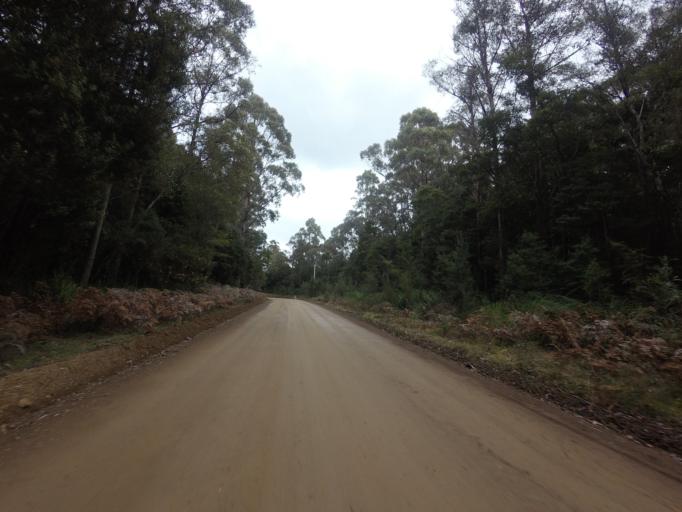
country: AU
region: Tasmania
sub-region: Huon Valley
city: Geeveston
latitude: -43.4131
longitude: 146.8996
